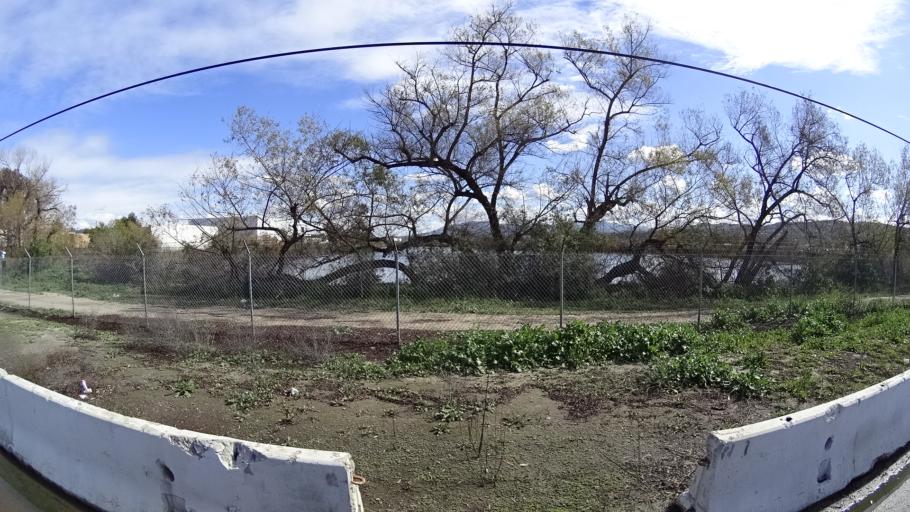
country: US
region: California
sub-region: Orange County
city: Yorba Linda
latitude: 33.8571
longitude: -117.8259
